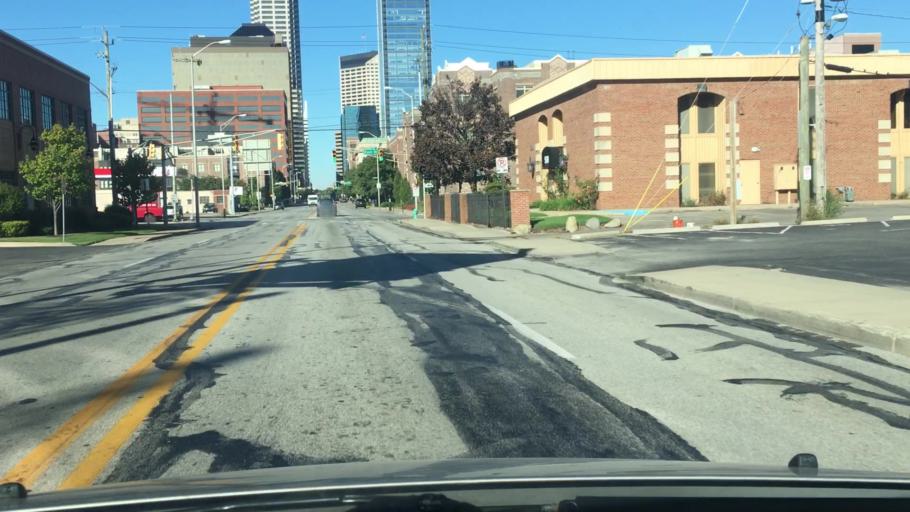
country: US
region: Indiana
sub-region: Marion County
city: Indianapolis
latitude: 39.7697
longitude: -86.1482
